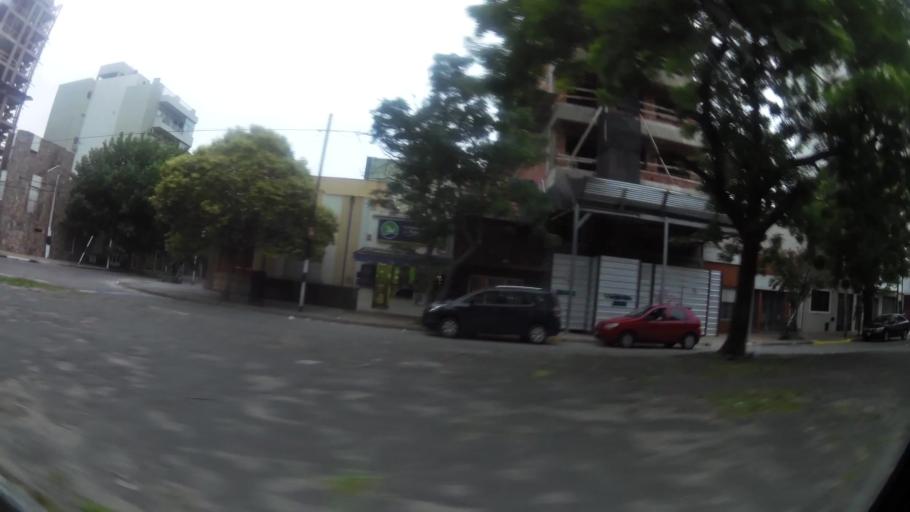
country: AR
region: Buenos Aires
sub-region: Partido de La Plata
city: La Plata
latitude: -34.9073
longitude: -57.9640
